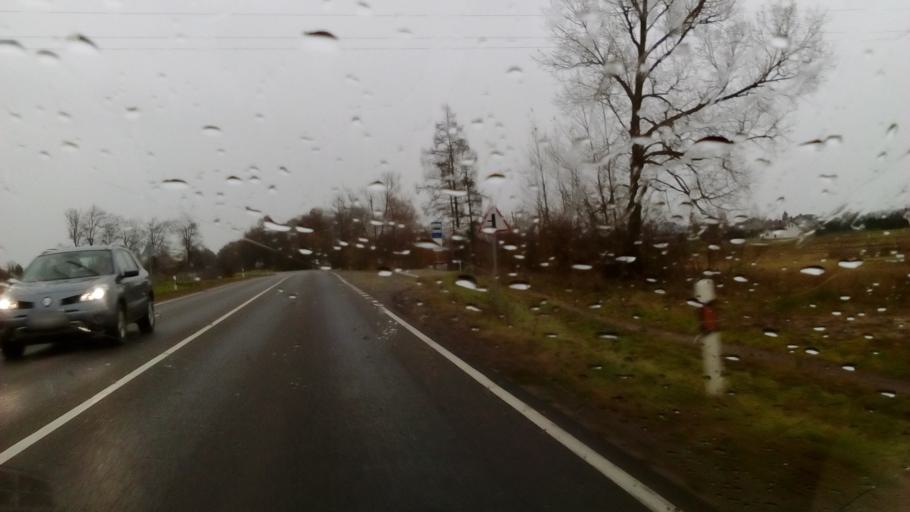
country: LT
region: Marijampoles apskritis
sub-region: Marijampole Municipality
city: Marijampole
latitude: 54.5492
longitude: 23.4082
